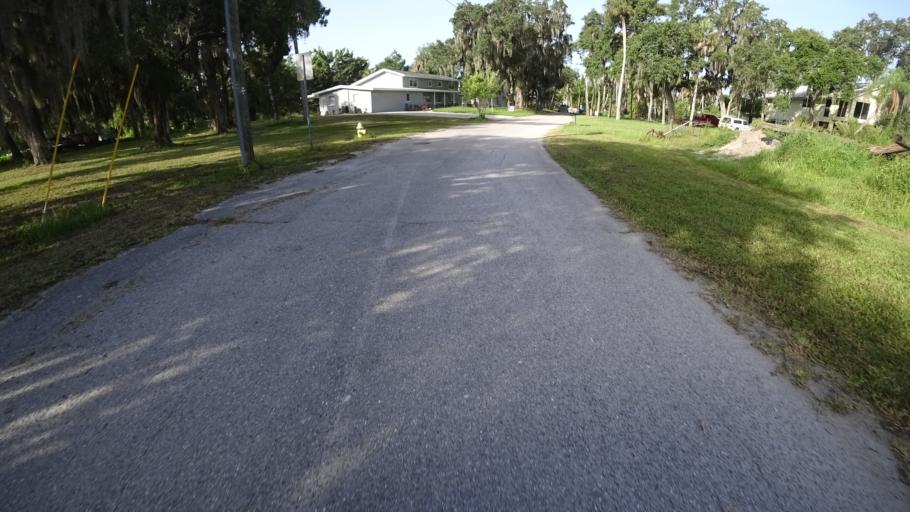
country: US
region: Florida
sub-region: Sarasota County
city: Desoto Lakes
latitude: 27.4217
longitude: -82.4782
